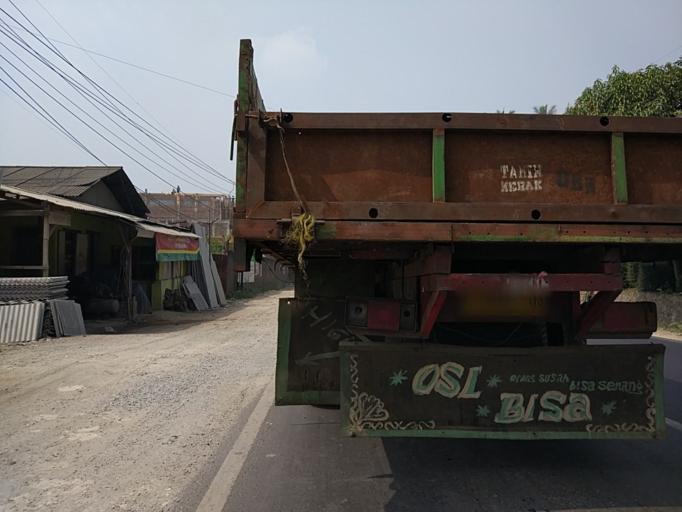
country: ID
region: West Java
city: Padalarang
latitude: -6.8329
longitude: 107.4661
